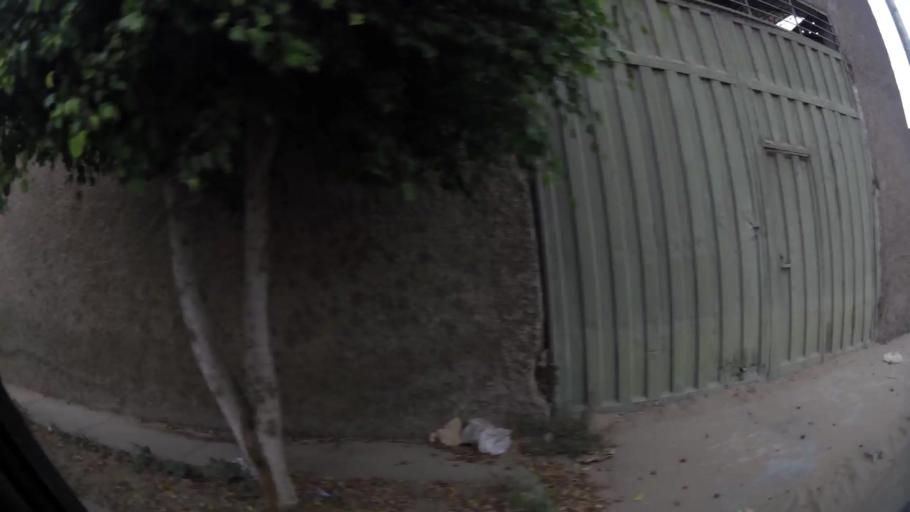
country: PE
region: La Libertad
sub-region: Provincia de Trujillo
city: La Esperanza
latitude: -8.0838
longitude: -79.0479
